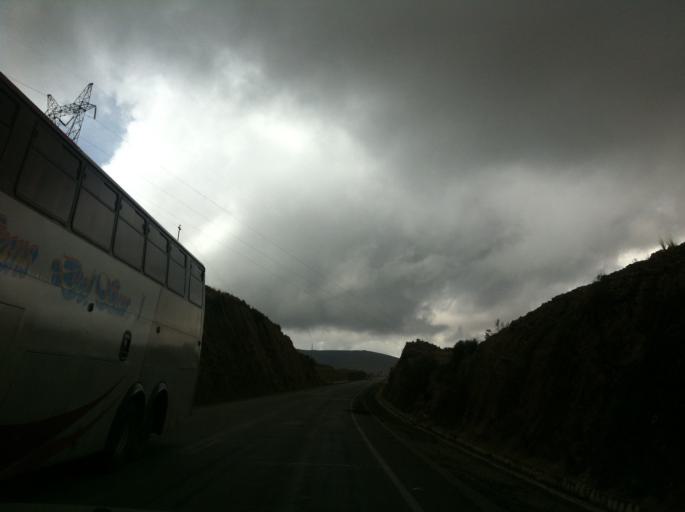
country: BO
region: Cochabamba
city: Irpa Irpa
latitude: -17.6973
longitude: -66.5191
